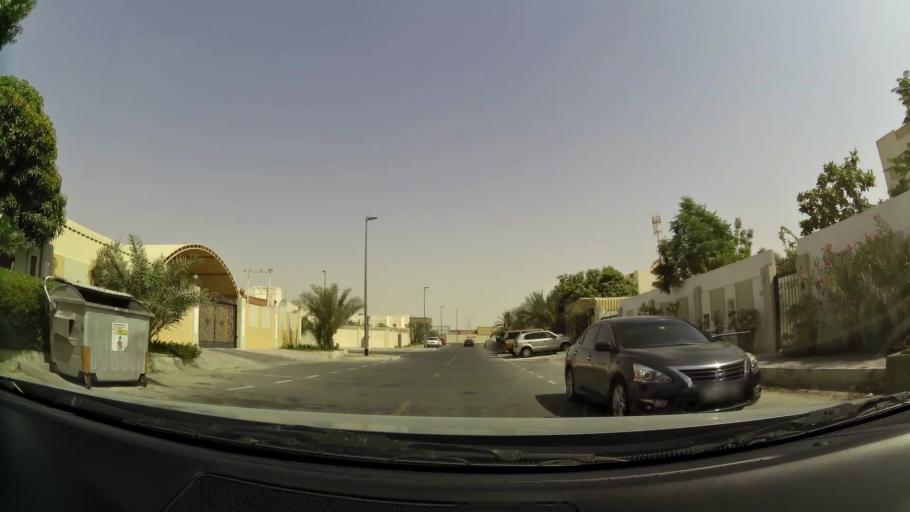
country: AE
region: Dubai
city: Dubai
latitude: 25.1500
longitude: 55.2549
